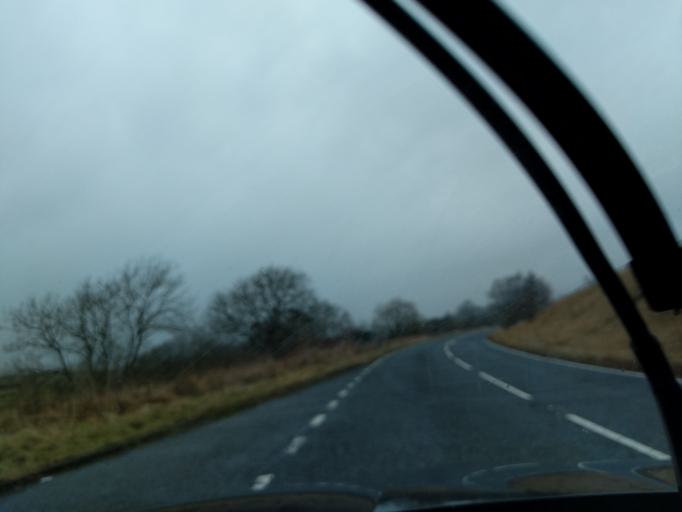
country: GB
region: England
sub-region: Northumberland
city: Otterburn
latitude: 55.2439
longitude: -2.2157
